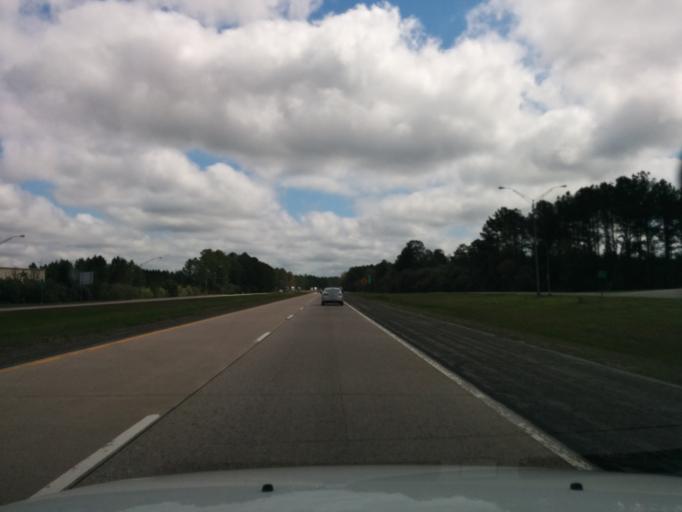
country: US
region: Georgia
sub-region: Chatham County
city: Bloomingdale
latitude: 32.1675
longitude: -81.4423
